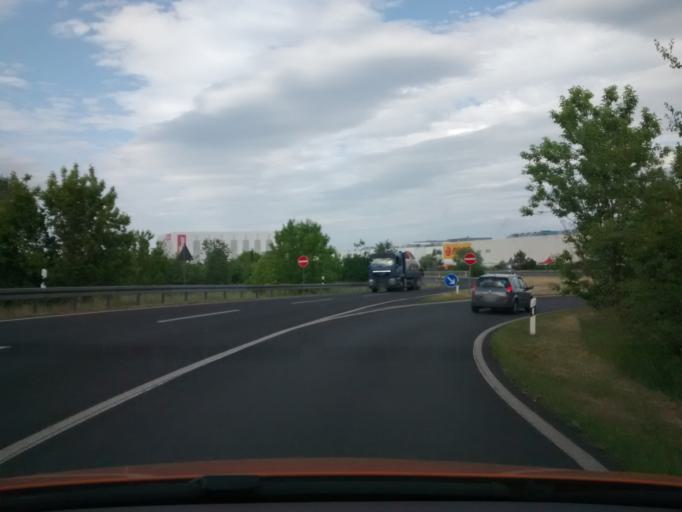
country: DE
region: Brandenburg
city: Schulzendorf
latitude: 52.3685
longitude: 13.5532
